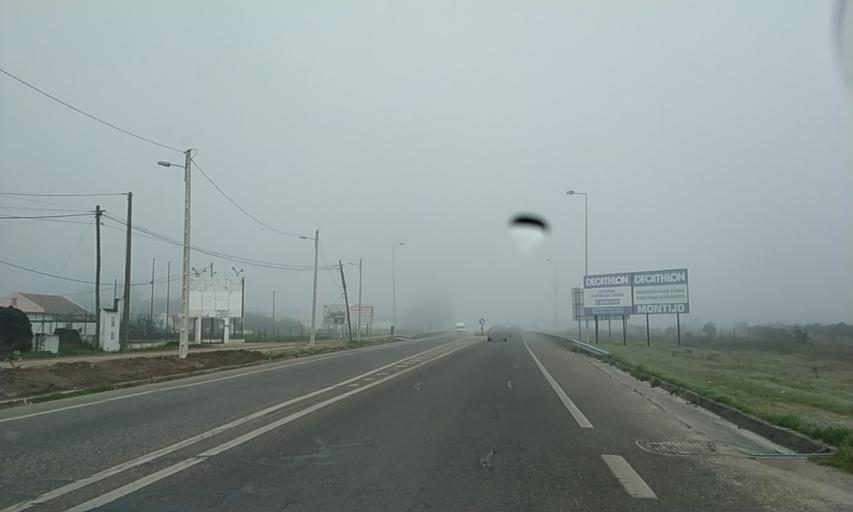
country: PT
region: Setubal
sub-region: Palmela
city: Pinhal Novo
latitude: 38.6480
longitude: -8.9154
